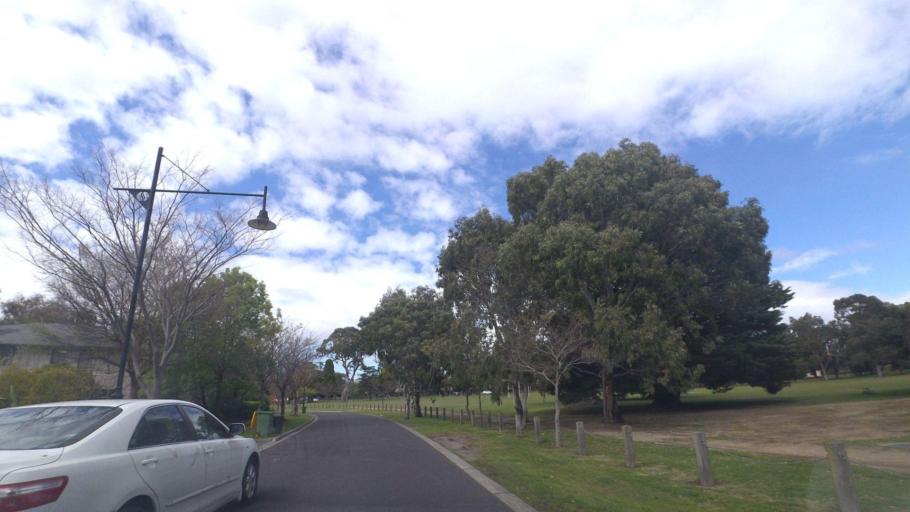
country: AU
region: Victoria
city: Macleod
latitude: -37.7204
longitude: 145.0599
